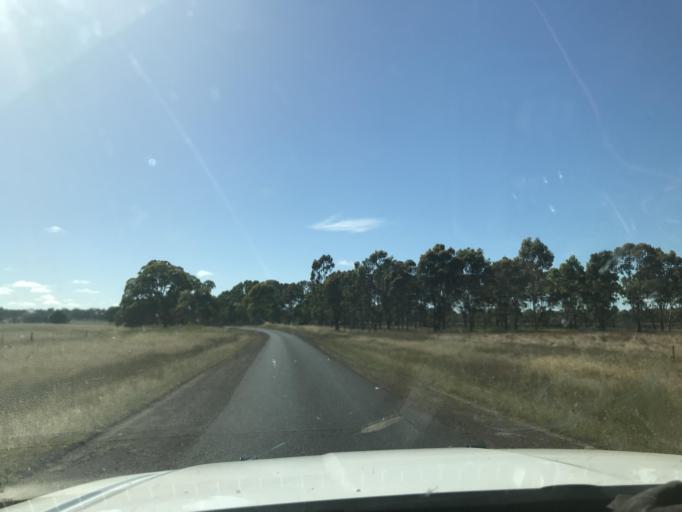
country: AU
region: Victoria
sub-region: Horsham
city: Horsham
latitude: -37.0868
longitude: 141.7561
